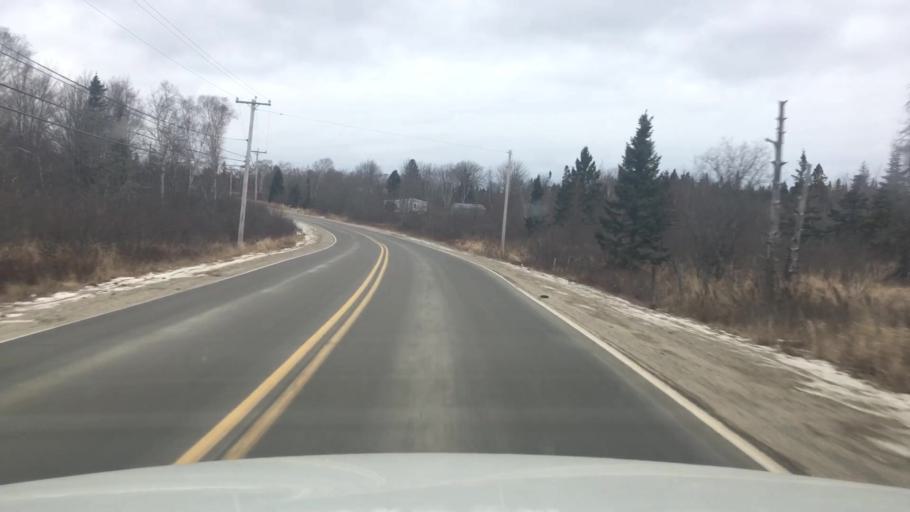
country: US
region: Maine
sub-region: Washington County
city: Jonesport
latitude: 44.5564
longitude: -67.6265
